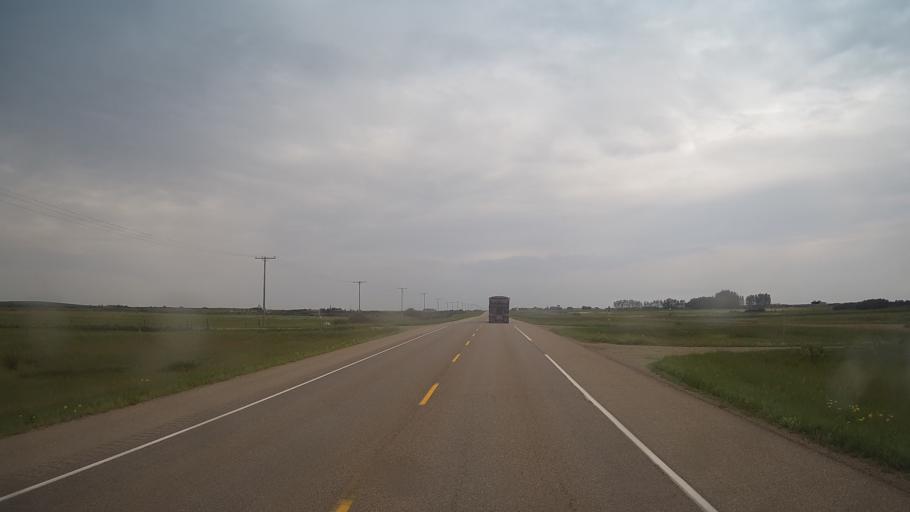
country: CA
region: Saskatchewan
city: Langham
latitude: 52.1290
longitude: -107.1686
